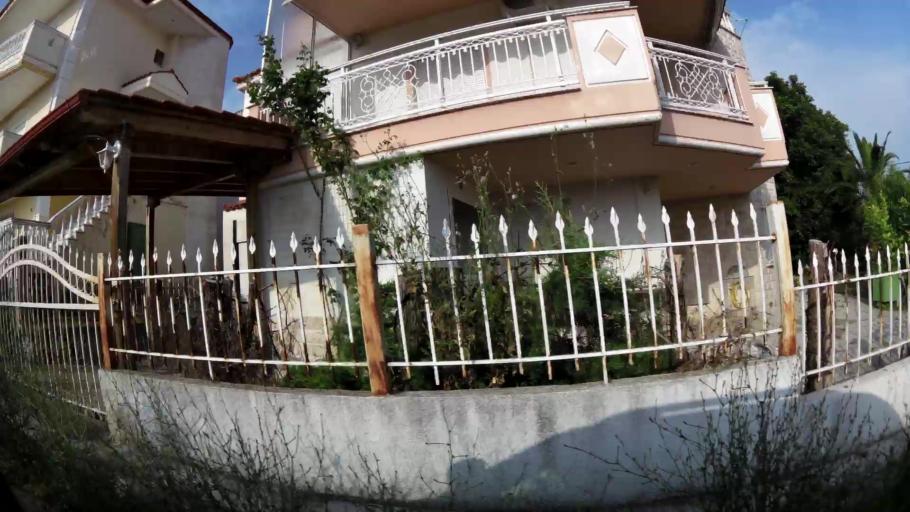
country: GR
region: Central Macedonia
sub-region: Nomos Thessalonikis
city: Oraiokastro
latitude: 40.7195
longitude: 22.9017
